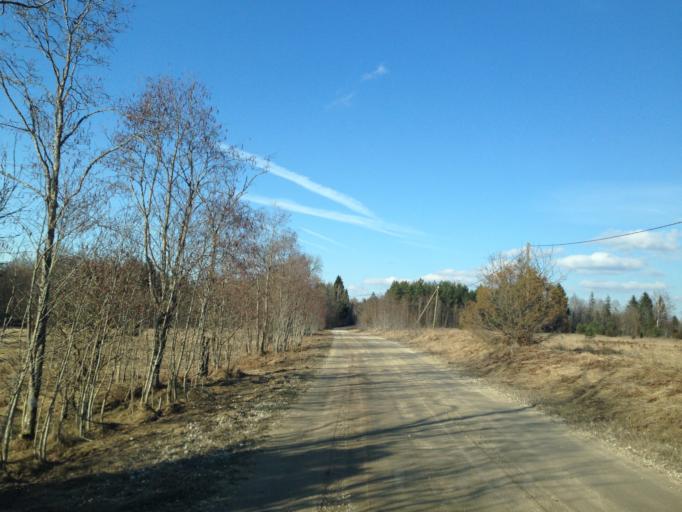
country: EE
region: Harju
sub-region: Nissi vald
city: Turba
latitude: 59.1133
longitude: 24.1583
